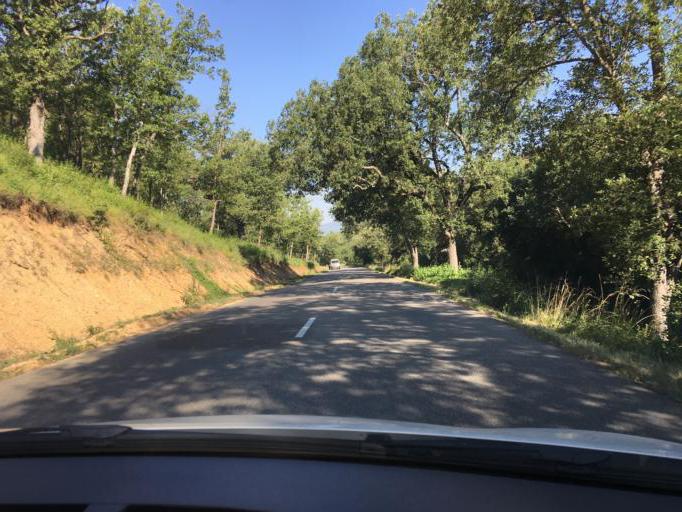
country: FR
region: Provence-Alpes-Cote d'Azur
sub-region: Departement des Alpes-de-Haute-Provence
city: Greoux-les-Bains
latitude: 43.7925
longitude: 5.8408
